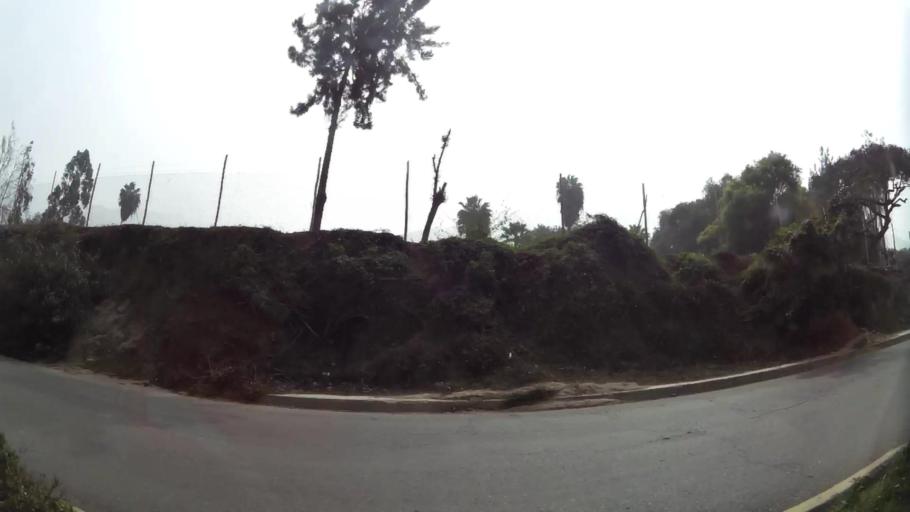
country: PE
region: Lima
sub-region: Lima
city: Chaclacayo
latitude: -11.9626
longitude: -76.7394
